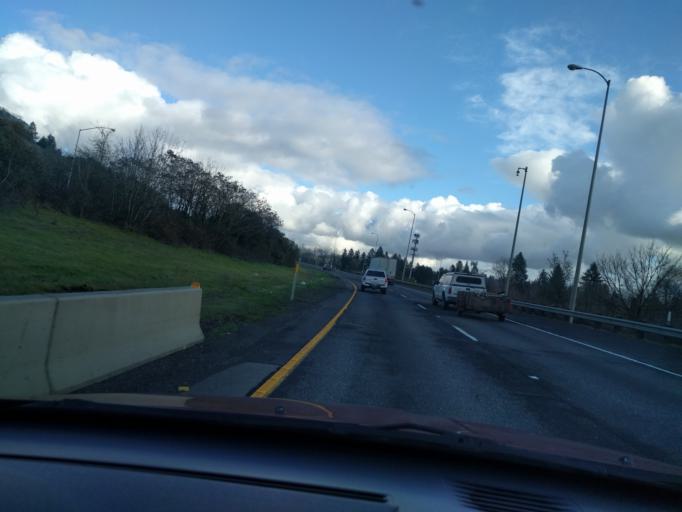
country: US
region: Oregon
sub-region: Clackamas County
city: West Linn
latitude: 45.3473
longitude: -122.6518
